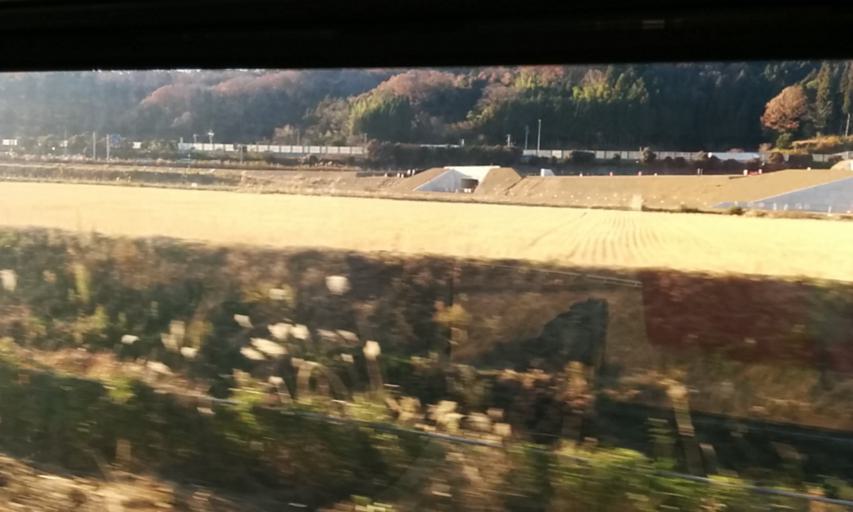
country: JP
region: Gifu
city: Mizunami
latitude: 35.3926
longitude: 137.2760
